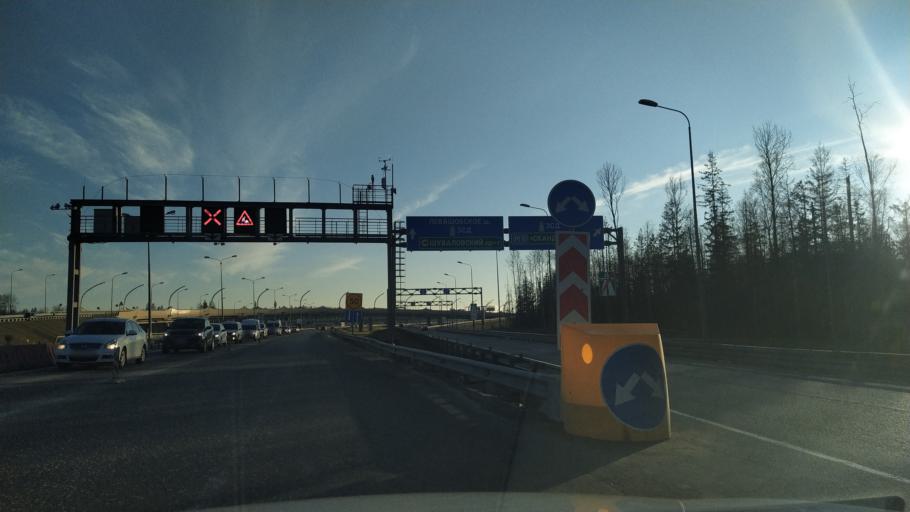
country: RU
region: St.-Petersburg
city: Pesochnyy
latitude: 60.0617
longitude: 30.1567
